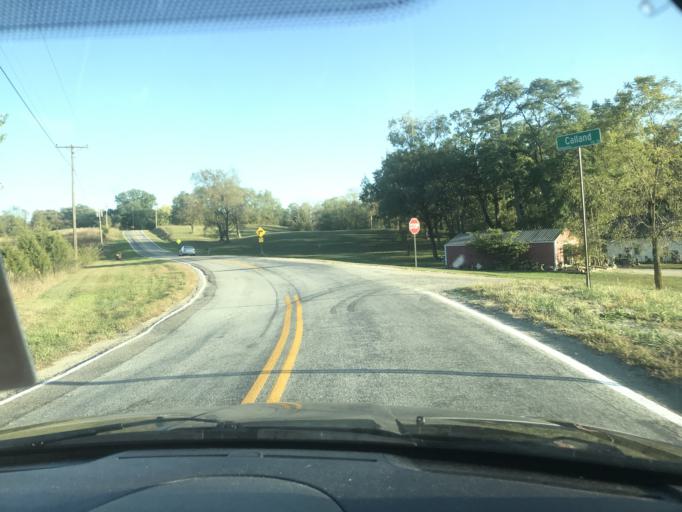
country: US
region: Ohio
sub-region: Logan County
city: De Graff
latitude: 40.2516
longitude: -83.8689
